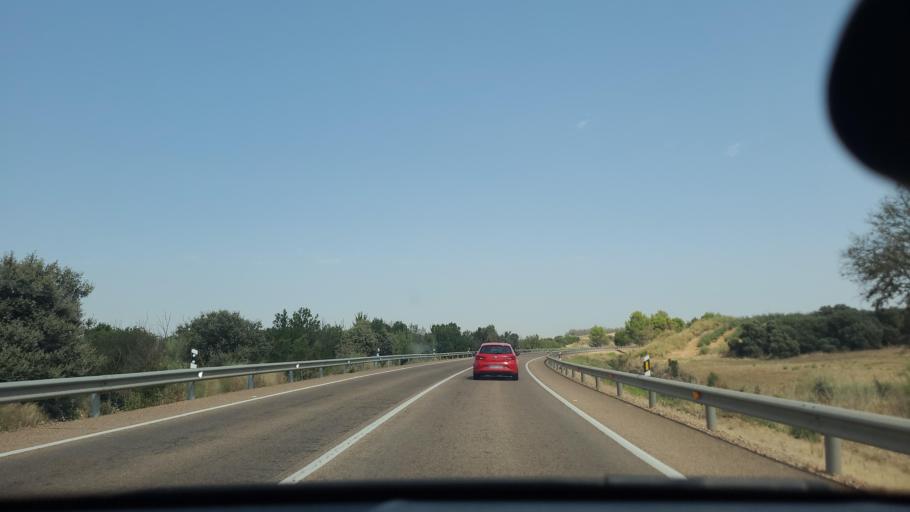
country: ES
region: Extremadura
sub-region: Provincia de Badajoz
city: La Albuera
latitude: 38.7746
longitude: -6.8570
